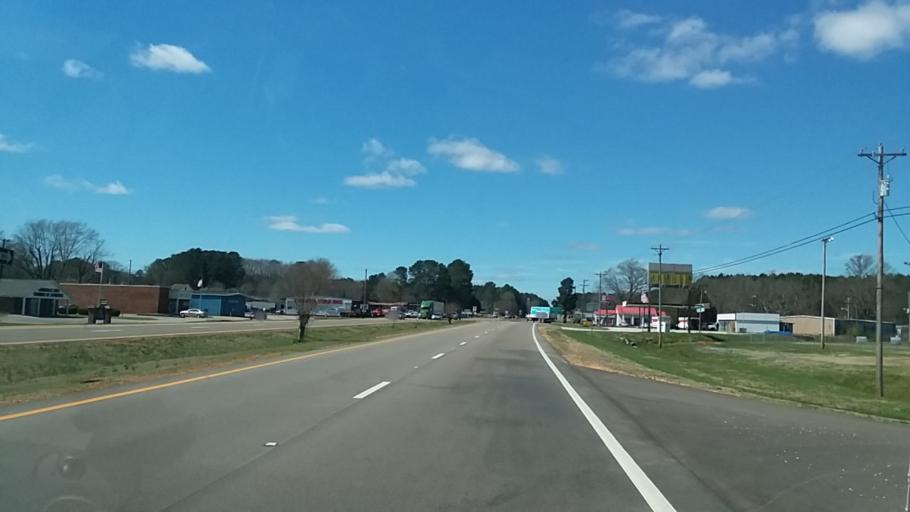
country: US
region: Mississippi
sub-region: Tishomingo County
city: Iuka
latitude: 34.8346
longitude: -88.3149
